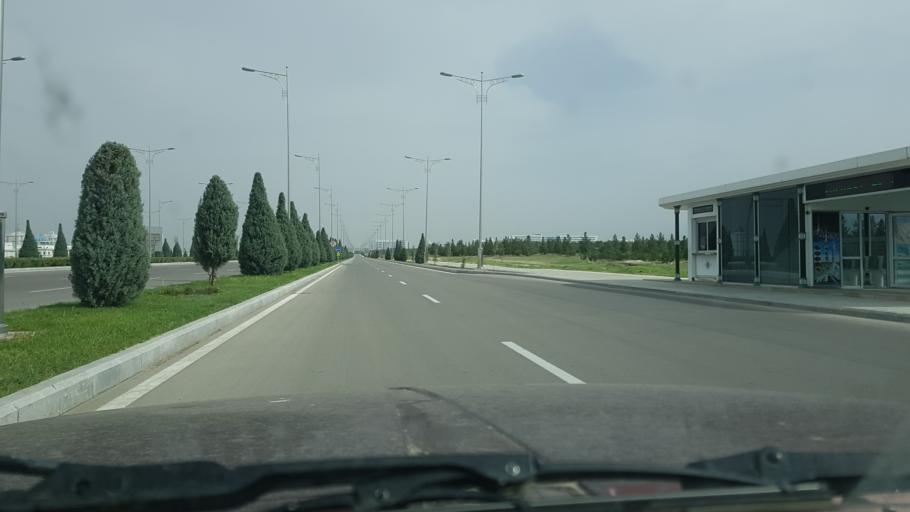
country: TM
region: Ahal
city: Ashgabat
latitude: 37.8868
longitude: 58.3388
